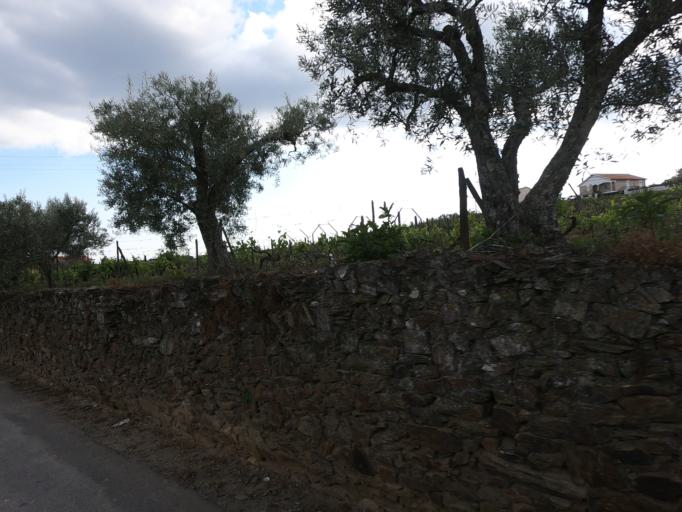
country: PT
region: Vila Real
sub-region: Sabrosa
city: Vilela
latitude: 41.2061
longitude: -7.6590
